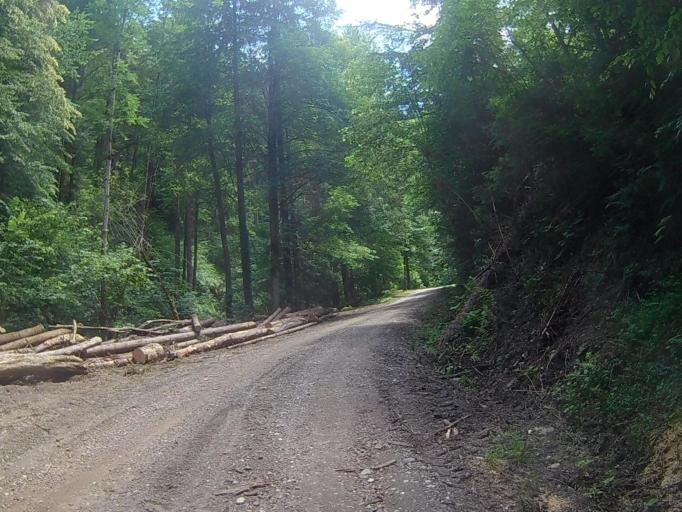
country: SI
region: Ruse
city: Ruse
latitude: 46.5286
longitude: 15.5022
